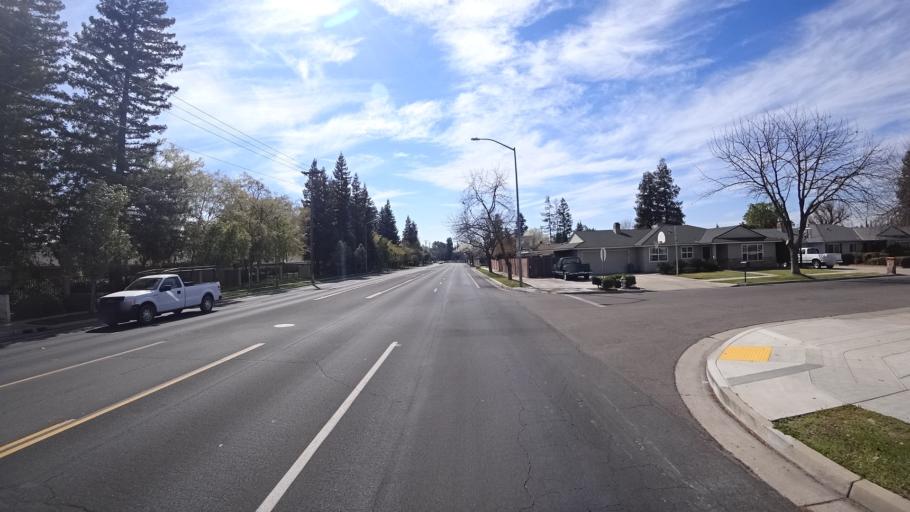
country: US
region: California
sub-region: Fresno County
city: Clovis
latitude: 36.8430
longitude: -119.7659
